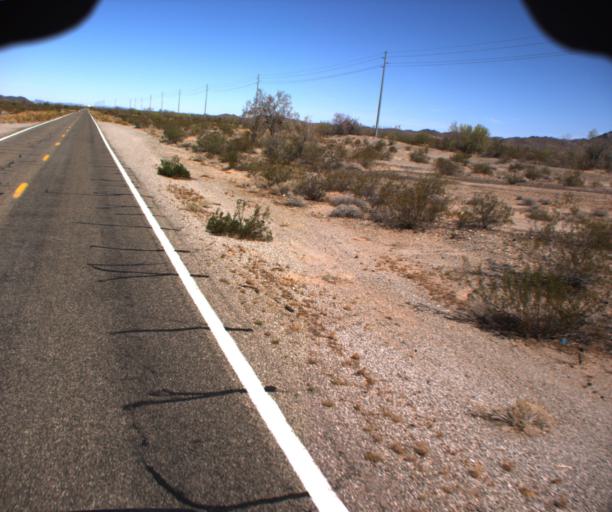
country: US
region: Arizona
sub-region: La Paz County
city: Salome
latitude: 33.7317
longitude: -113.7212
